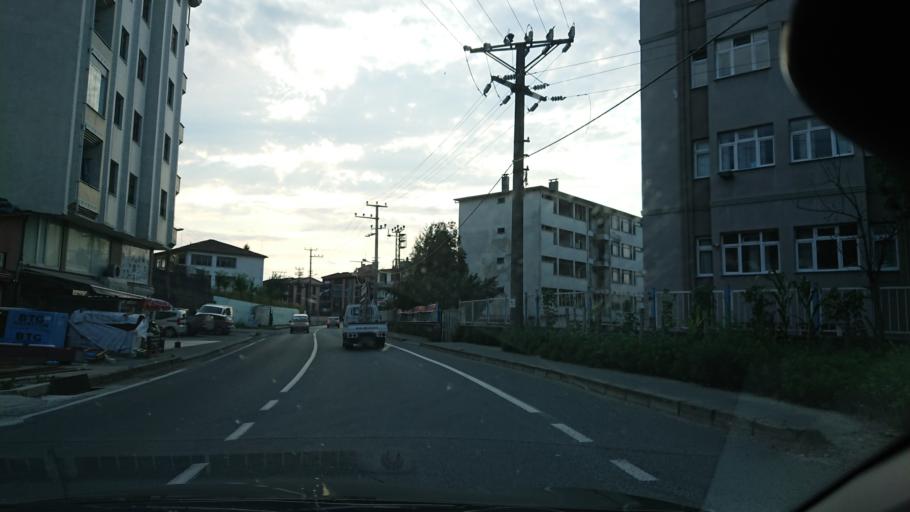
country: TR
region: Rize
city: Cayeli
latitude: 41.0822
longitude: 40.7112
